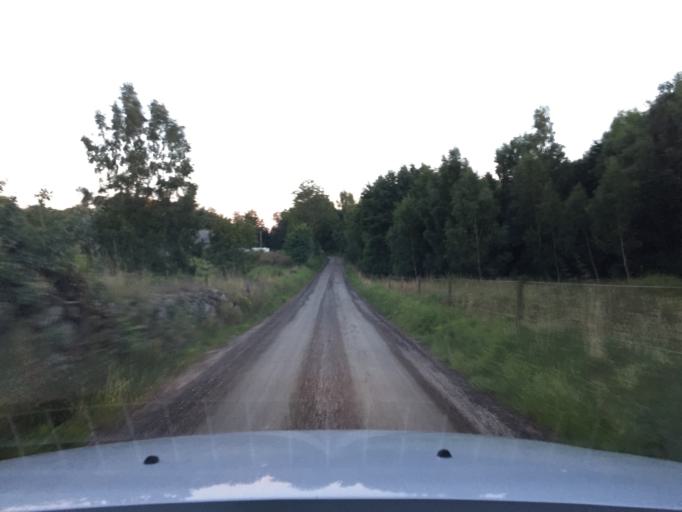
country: SE
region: Skane
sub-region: Hassleholms Kommun
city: Sosdala
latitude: 55.9984
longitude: 13.6668
